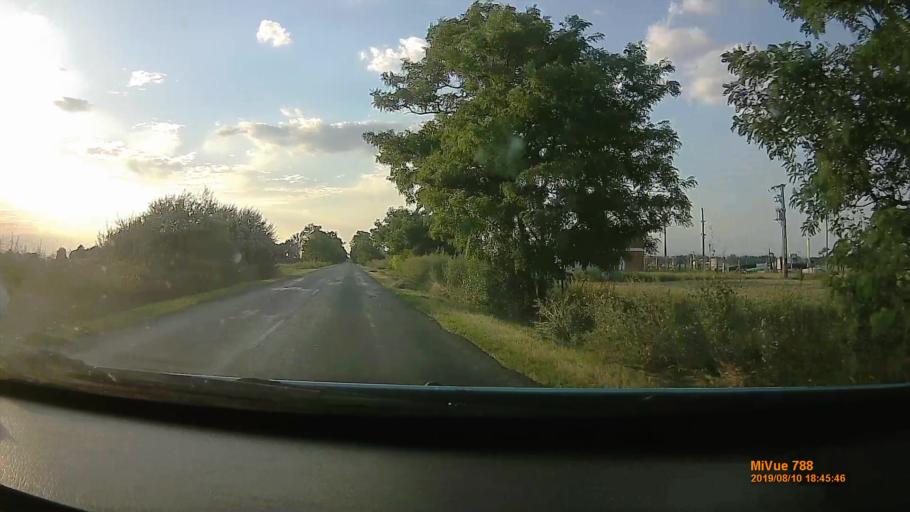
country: HU
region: Borsod-Abauj-Zemplen
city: Mezokovesd
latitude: 47.7690
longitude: 20.5943
